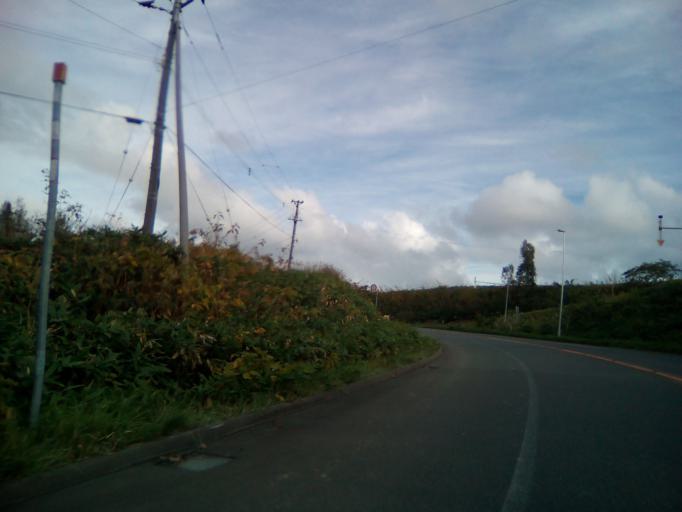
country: JP
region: Hokkaido
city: Niseko Town
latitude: 42.6791
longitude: 140.8361
